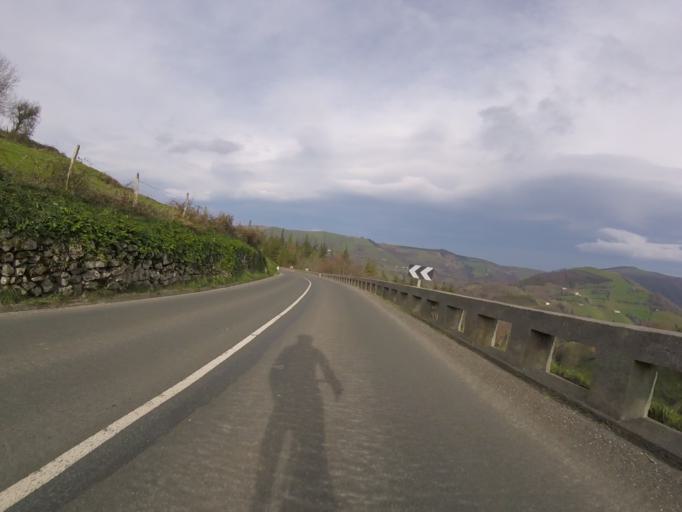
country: ES
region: Basque Country
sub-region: Provincia de Guipuzcoa
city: Beizama
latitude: 43.1676
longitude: -2.2218
